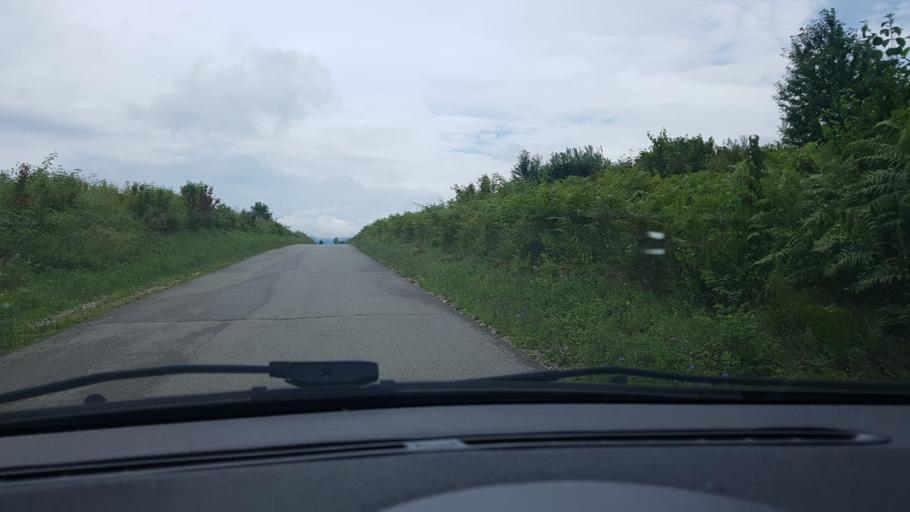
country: BA
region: Federation of Bosnia and Herzegovina
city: Trzacka Rastela
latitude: 44.9655
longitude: 15.6876
